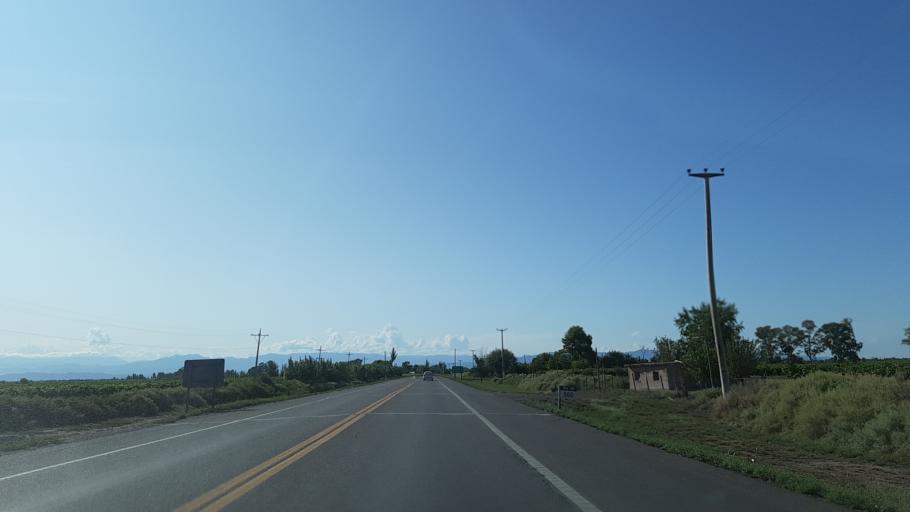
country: AR
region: San Juan
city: Caucete
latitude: -31.6202
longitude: -68.3104
